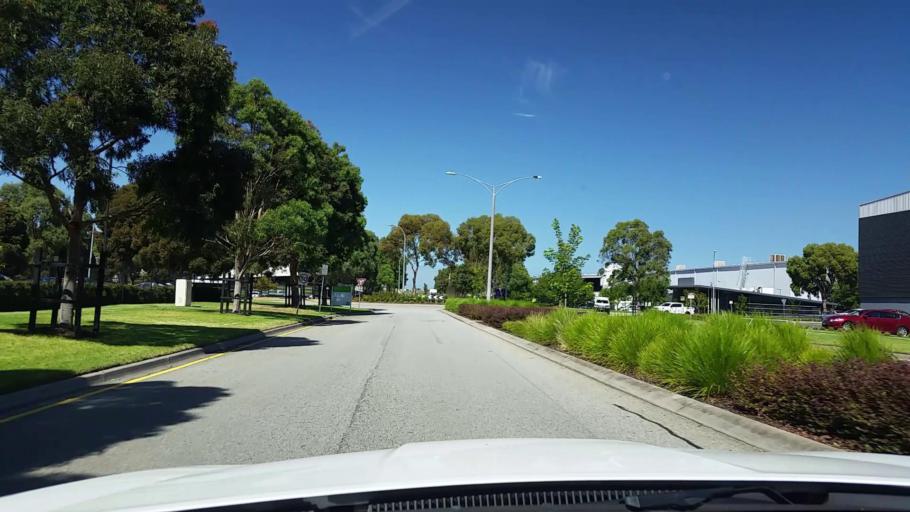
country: AU
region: Victoria
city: Heatherton
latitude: -37.9730
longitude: 145.1068
